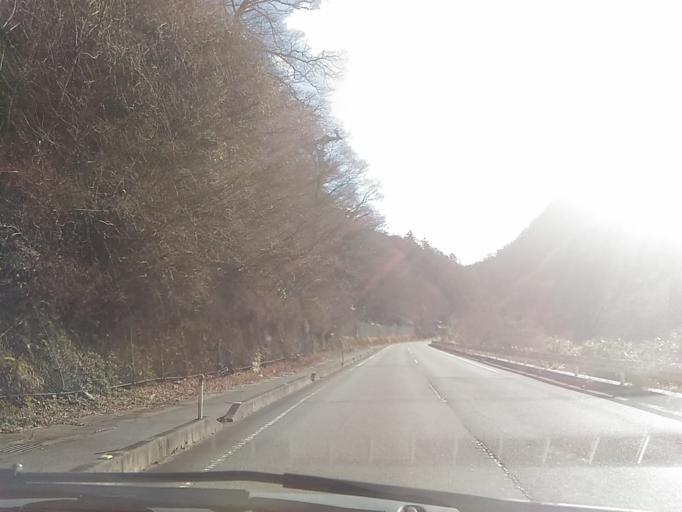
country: JP
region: Fukushima
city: Iwaki
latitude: 37.0122
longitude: 140.6820
